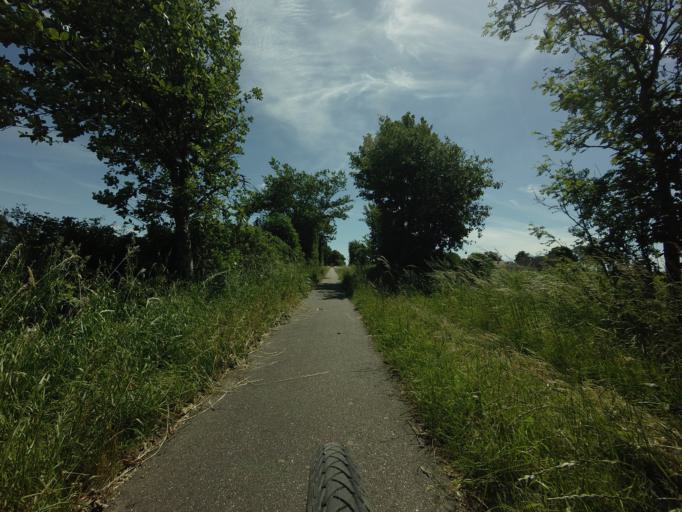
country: DK
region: Central Jutland
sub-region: Horsens Kommune
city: Braedstrup
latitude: 56.0129
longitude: 9.5847
